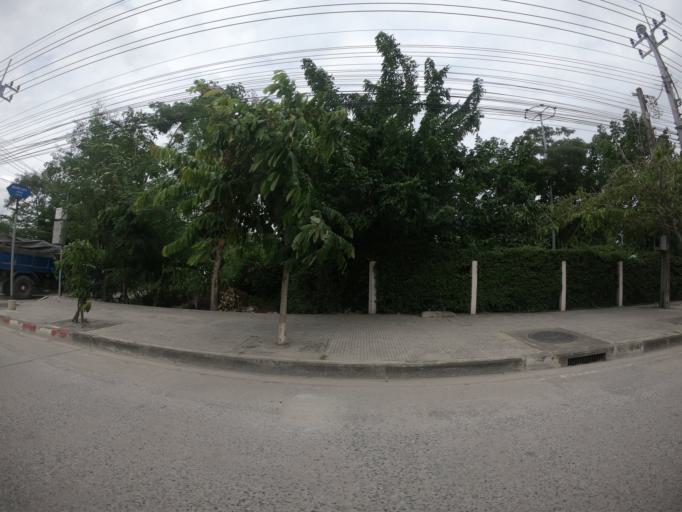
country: TH
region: Bangkok
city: Bang Na
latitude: 13.6776
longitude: 100.6775
